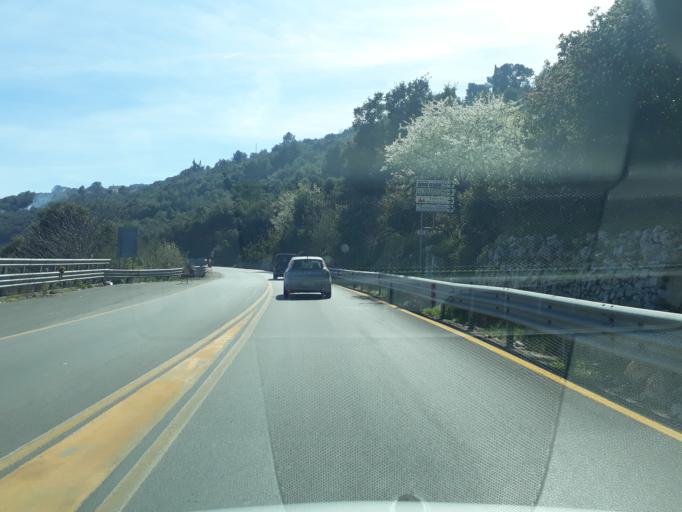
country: IT
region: Apulia
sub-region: Provincia di Brindisi
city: Lamie di Olimpie-Selva
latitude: 40.8100
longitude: 17.3448
